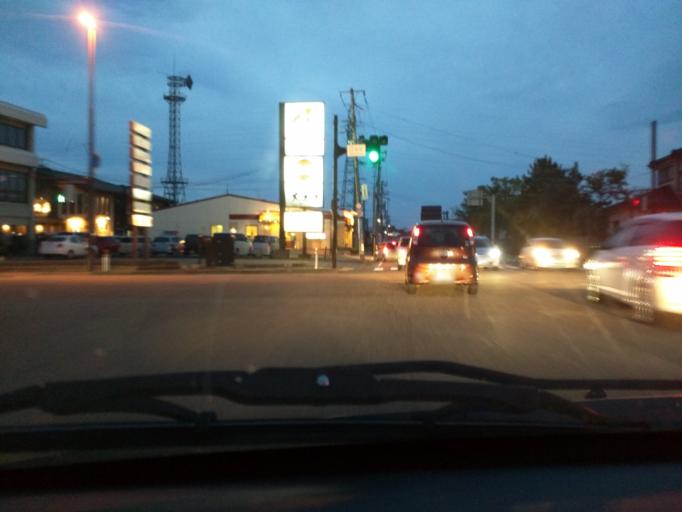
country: JP
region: Niigata
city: Kashiwazaki
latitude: 37.3674
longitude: 138.5753
